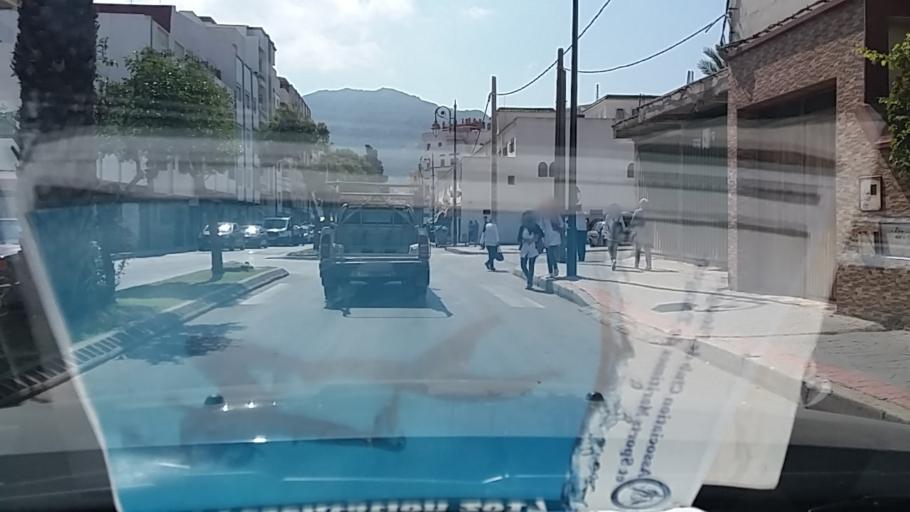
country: MA
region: Tanger-Tetouan
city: Tetouan
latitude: 35.5650
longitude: -5.3585
